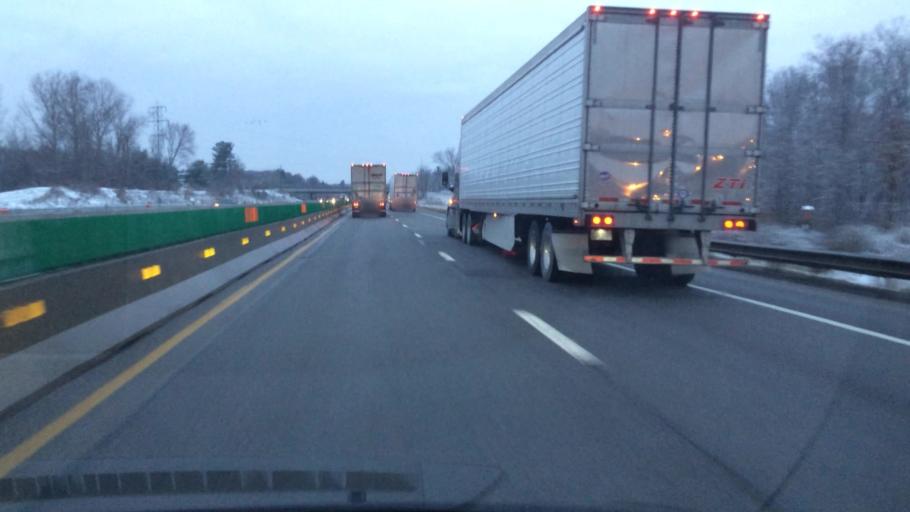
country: US
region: Ohio
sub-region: Summit County
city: Richfield
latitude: 41.2786
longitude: -81.6441
